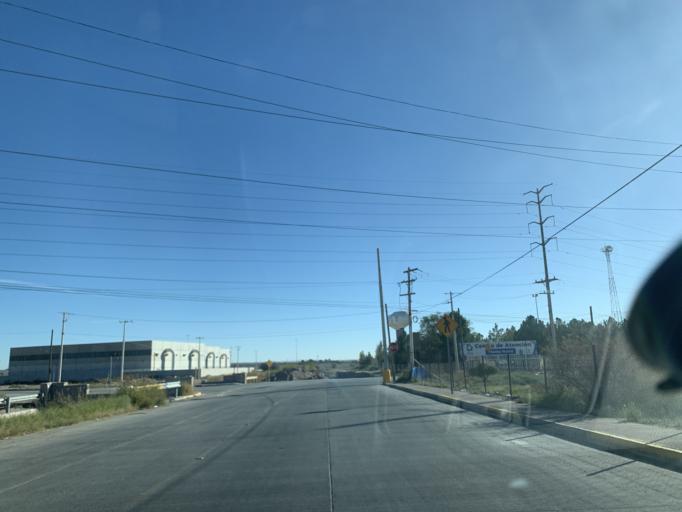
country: US
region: Texas
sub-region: El Paso County
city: Socorro
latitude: 31.7091
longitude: -106.3765
